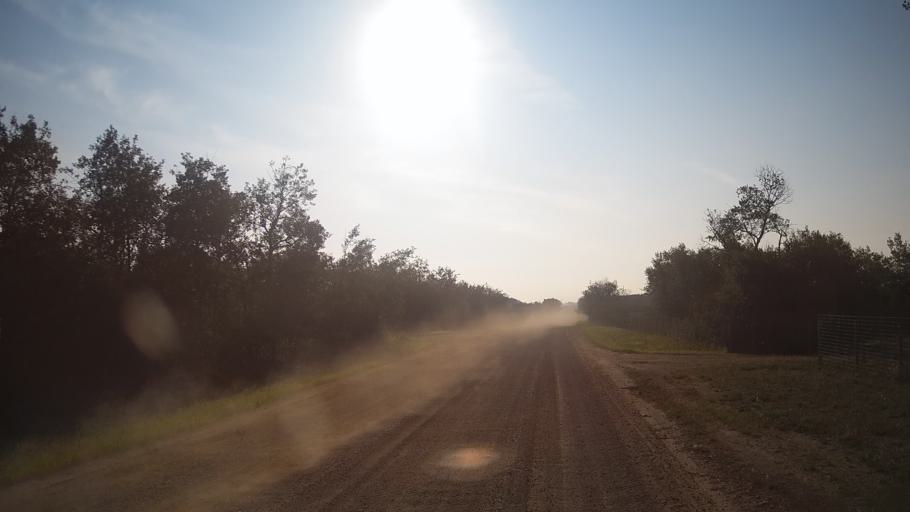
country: CA
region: Saskatchewan
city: Saskatoon
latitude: 51.8237
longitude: -106.5370
